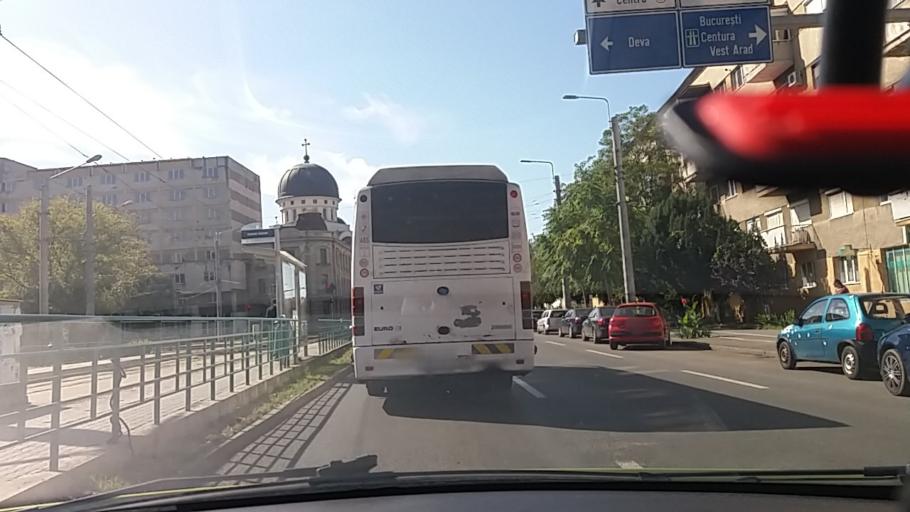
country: RO
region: Arad
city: Arad
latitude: 46.1857
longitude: 21.3249
